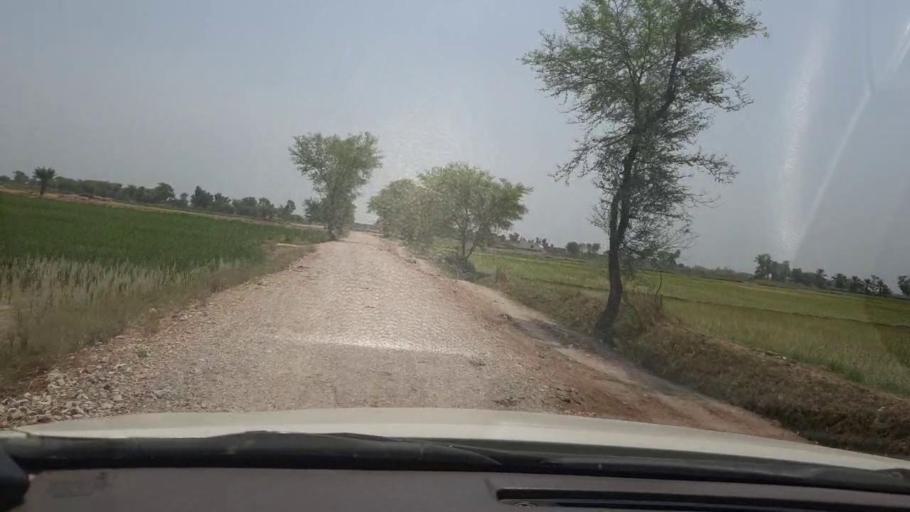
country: PK
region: Sindh
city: Garhi Yasin
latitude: 27.9145
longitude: 68.5567
